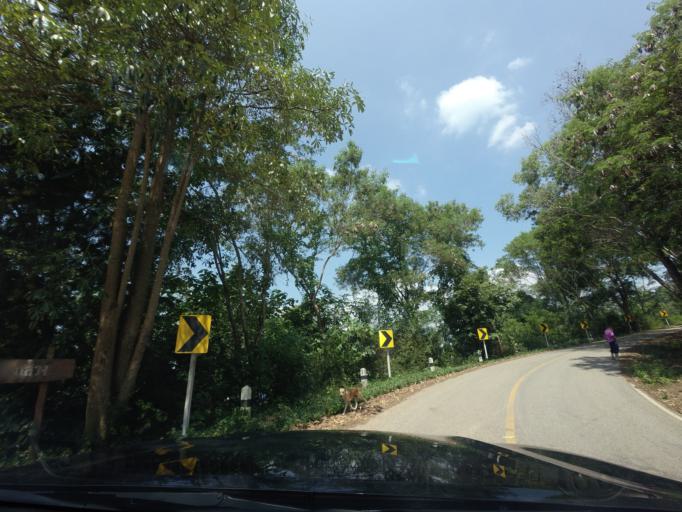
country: TH
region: Loei
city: Na Haeo
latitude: 17.6056
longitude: 100.8931
